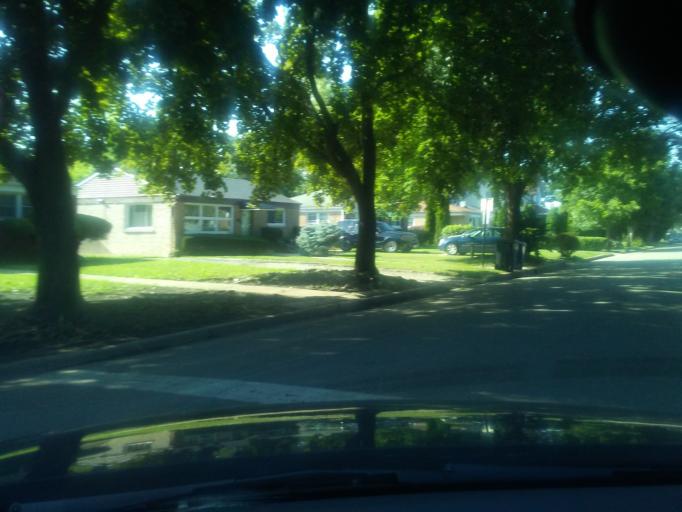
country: US
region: Illinois
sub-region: Cook County
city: Evanston
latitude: 42.0428
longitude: -87.7038
